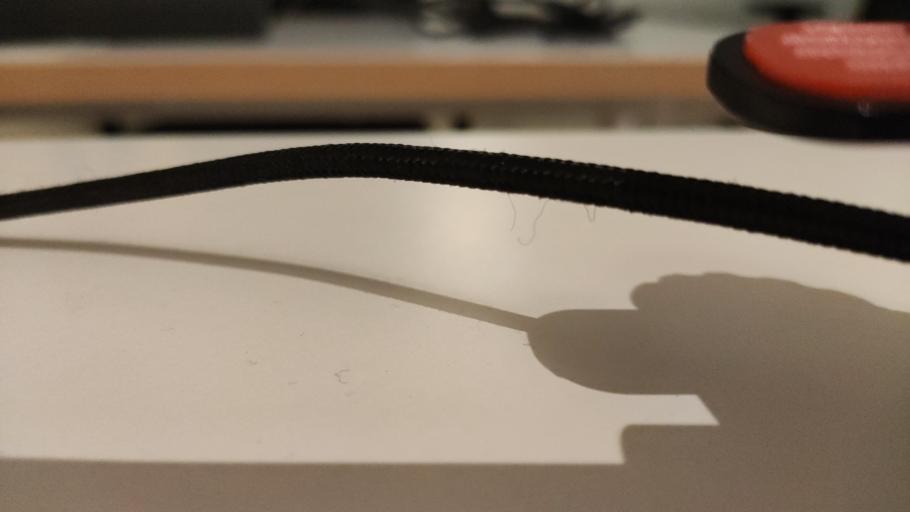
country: RU
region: Moskovskaya
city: Kurovskoye
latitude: 55.5384
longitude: 38.8729
